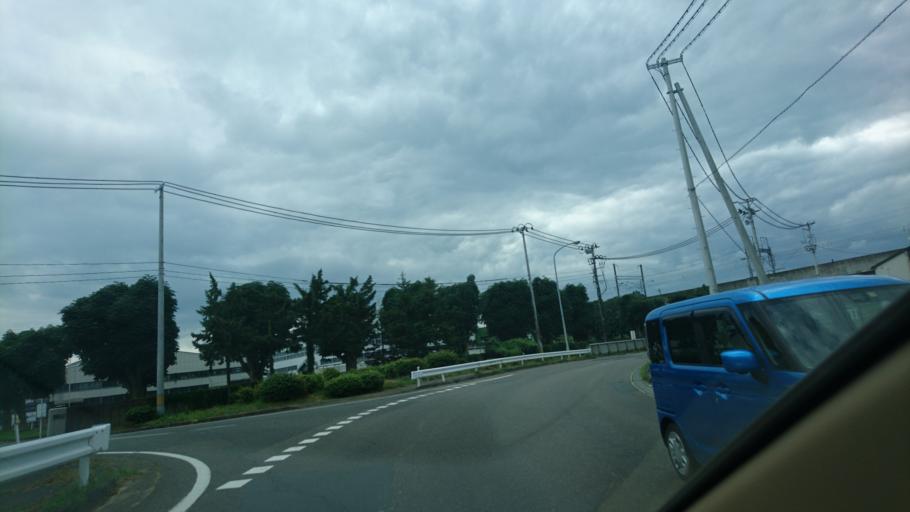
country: JP
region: Iwate
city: Kitakami
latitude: 39.2773
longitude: 141.1221
